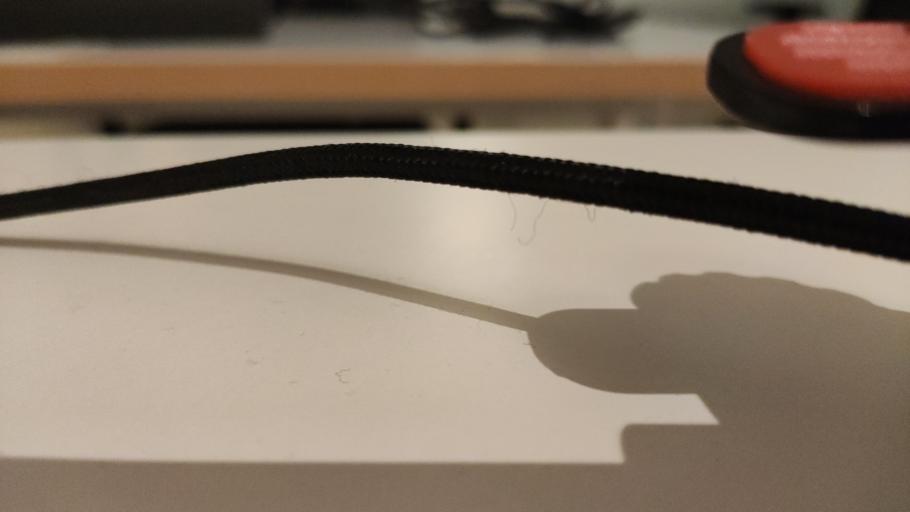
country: RU
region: Moskovskaya
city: Shaburnovo
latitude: 56.4370
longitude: 37.9176
